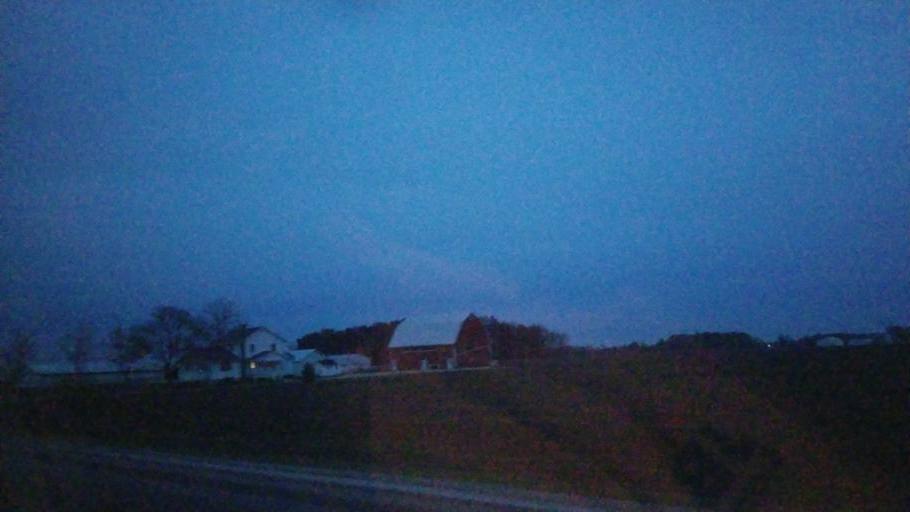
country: US
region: Indiana
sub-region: Adams County
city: Berne
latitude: 40.6873
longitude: -84.9559
